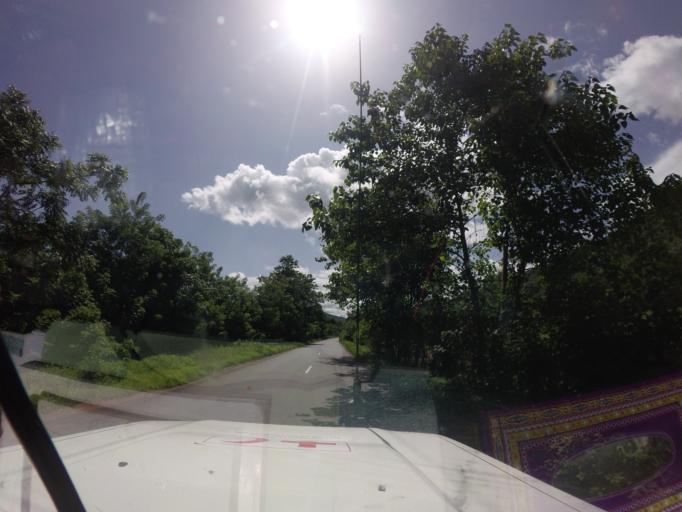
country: GN
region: Mamou
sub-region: Mamou Prefecture
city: Mamou
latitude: 10.2276
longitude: -11.8618
